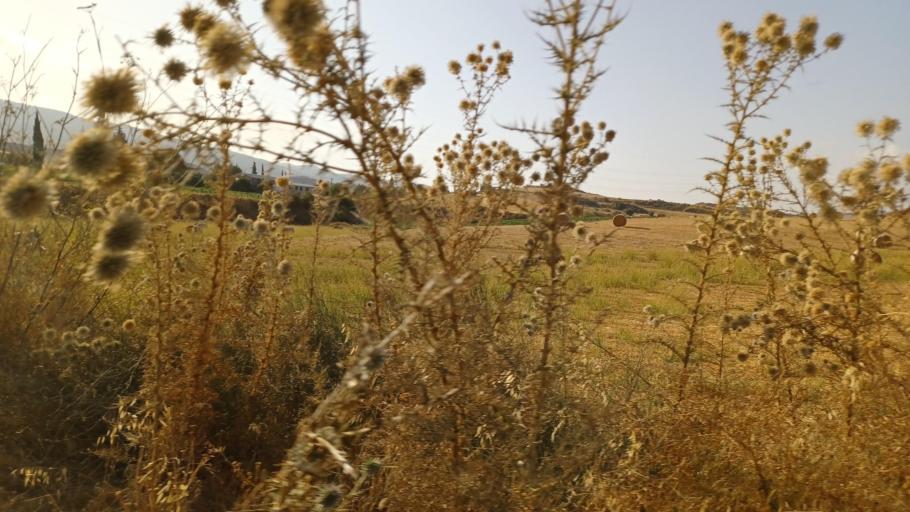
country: CY
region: Pafos
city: Polis
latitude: 35.0221
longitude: 32.4431
